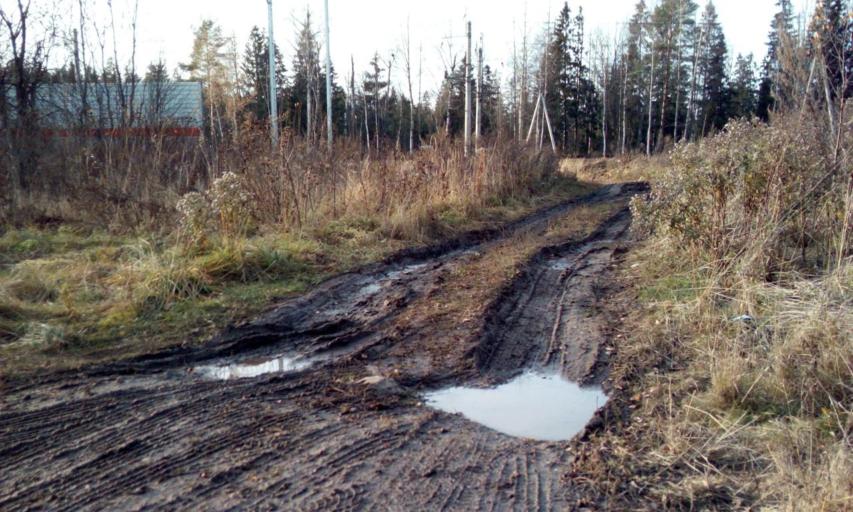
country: RU
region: Moskovskaya
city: Aprelevka
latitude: 55.5724
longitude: 37.1006
